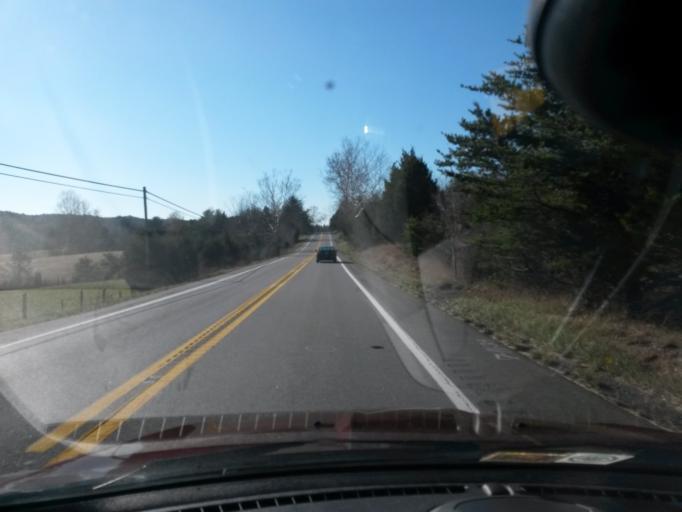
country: US
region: Virginia
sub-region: Alleghany County
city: Clifton Forge
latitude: 37.7278
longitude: -79.8030
